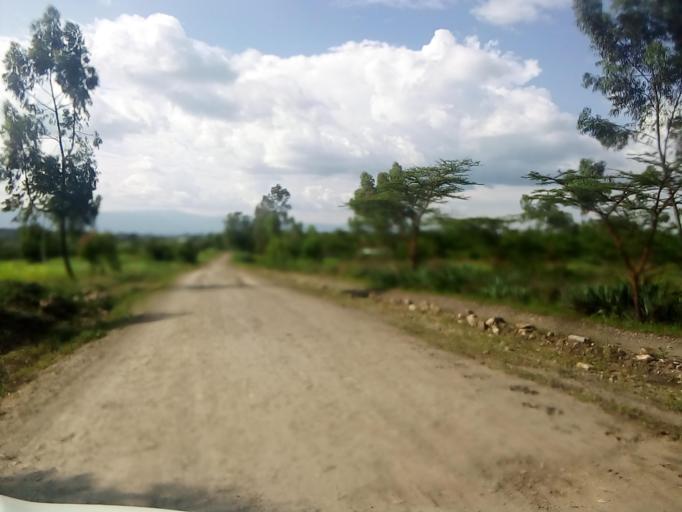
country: ET
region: Southern Nations, Nationalities, and People's Region
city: K'olito
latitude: 7.6478
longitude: 38.0520
